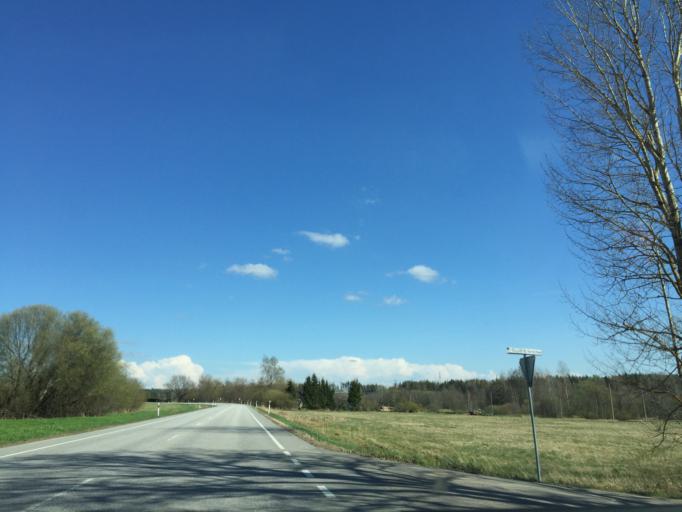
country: EE
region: Valgamaa
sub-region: Valga linn
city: Valga
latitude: 57.8529
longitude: 26.1563
